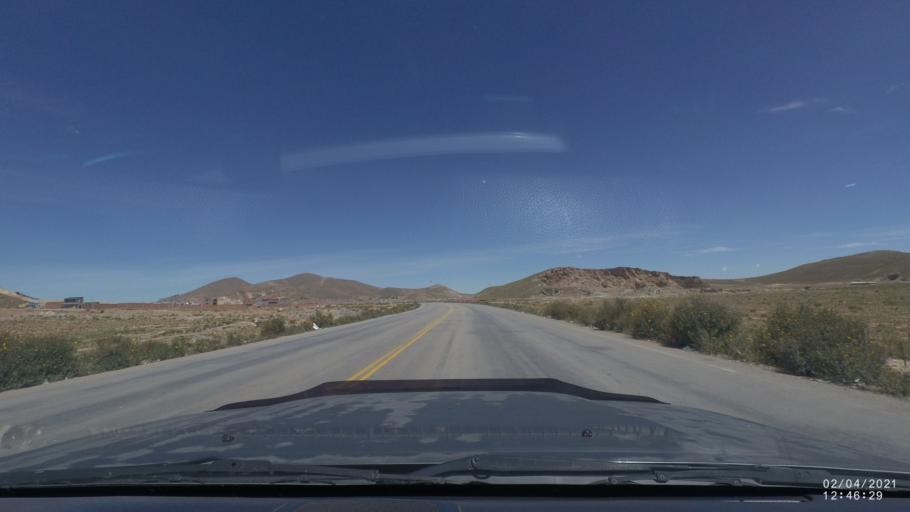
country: BO
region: Oruro
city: Oruro
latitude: -17.9455
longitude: -67.1427
